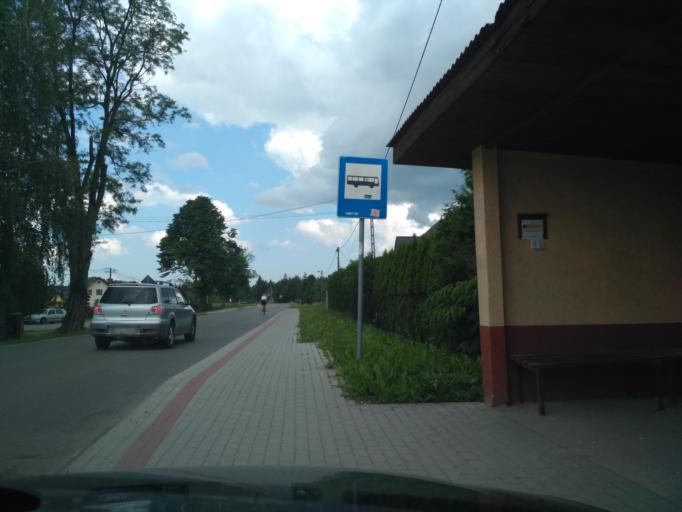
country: PL
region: Subcarpathian Voivodeship
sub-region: Powiat rzeszowski
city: Blazowa
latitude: 49.9111
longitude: 22.0909
